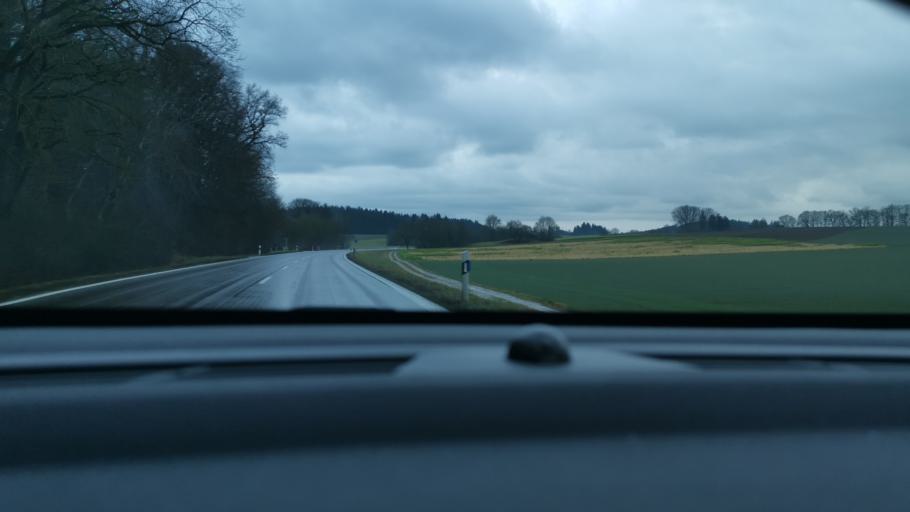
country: DE
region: Bavaria
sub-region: Swabia
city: Affing
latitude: 48.4858
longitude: 11.0074
